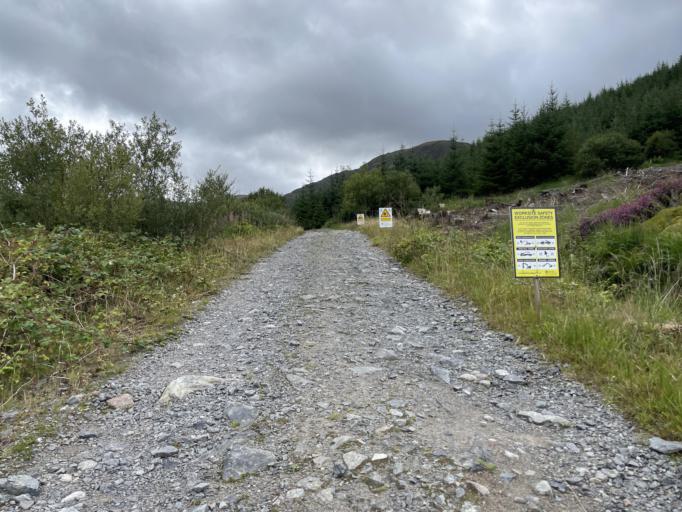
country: GB
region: Scotland
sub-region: Dumfries and Galloway
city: Newton Stewart
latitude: 55.0861
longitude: -4.4565
